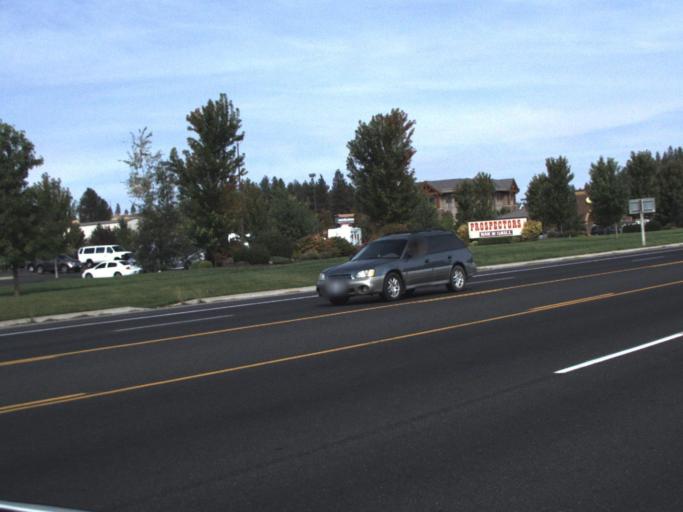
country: US
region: Washington
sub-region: Spokane County
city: Fairwood
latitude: 47.7719
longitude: -117.4035
